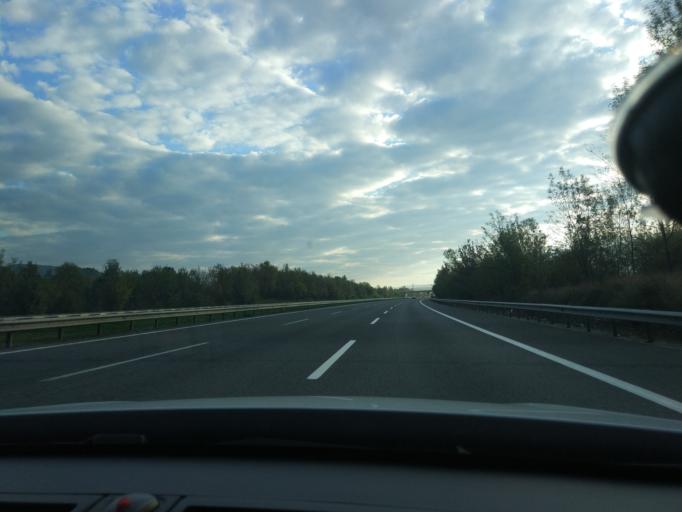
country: TR
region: Sakarya
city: Karadere
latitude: 40.7852
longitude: 30.8124
